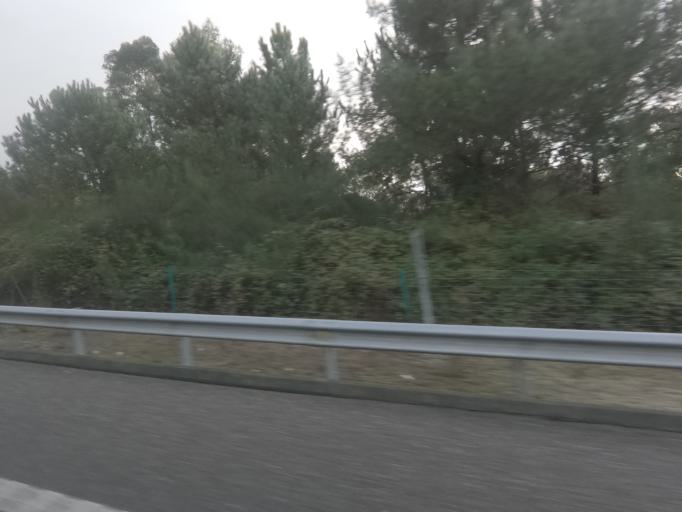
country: ES
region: Galicia
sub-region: Provincia de Pontevedra
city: Porrino
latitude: 42.1809
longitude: -8.6508
